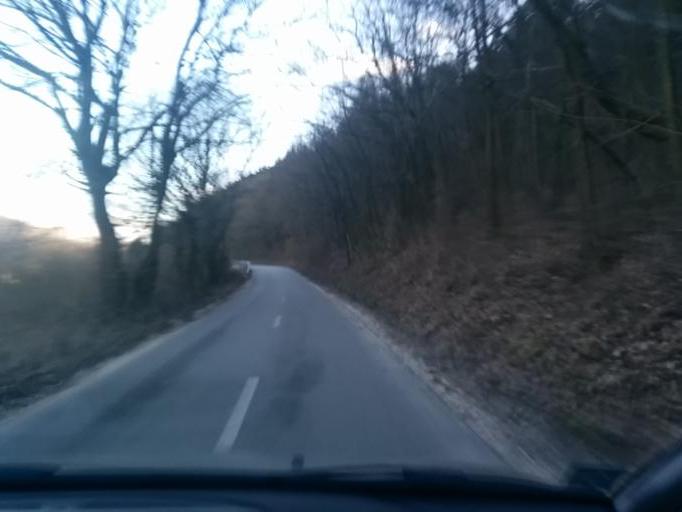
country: SK
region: Nitriansky
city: Cachtice
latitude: 48.7277
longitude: 17.7756
